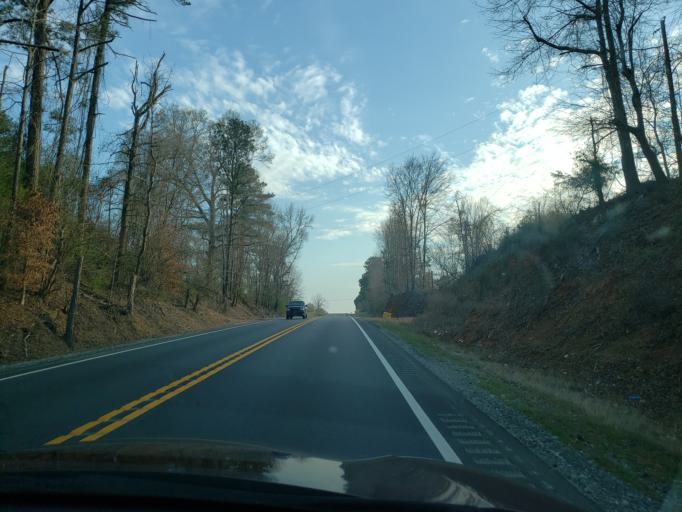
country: US
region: Alabama
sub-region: Hale County
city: Moundville
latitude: 32.8810
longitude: -87.6087
